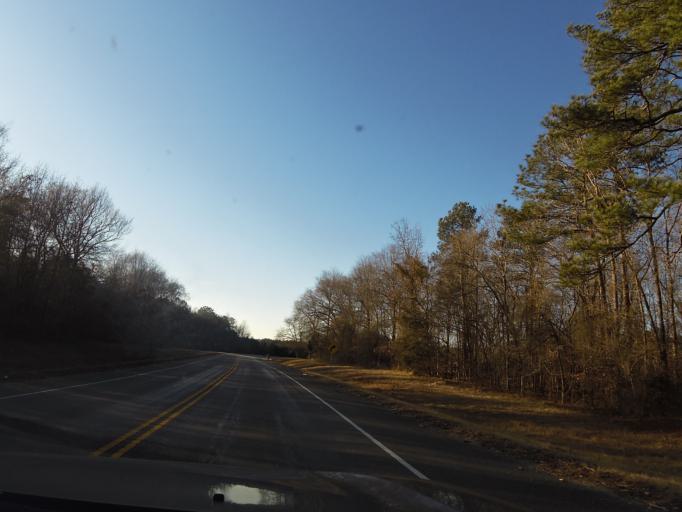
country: US
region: Virginia
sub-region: City of Franklin
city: Franklin
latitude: 36.6707
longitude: -76.8927
